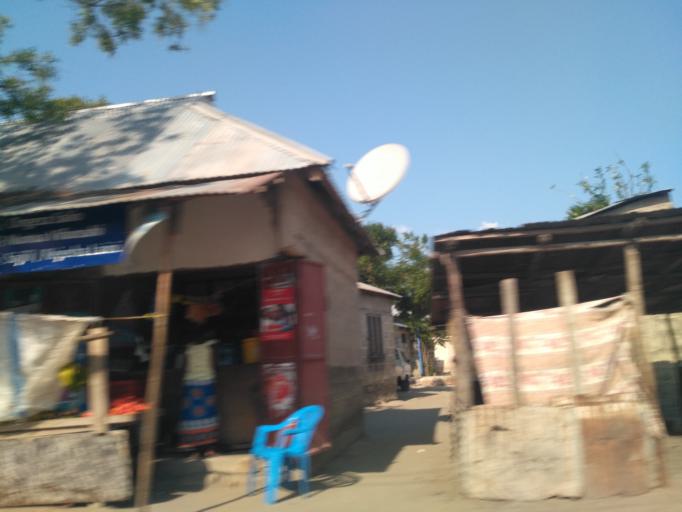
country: TZ
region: Dar es Salaam
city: Dar es Salaam
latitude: -6.8594
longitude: 39.3105
